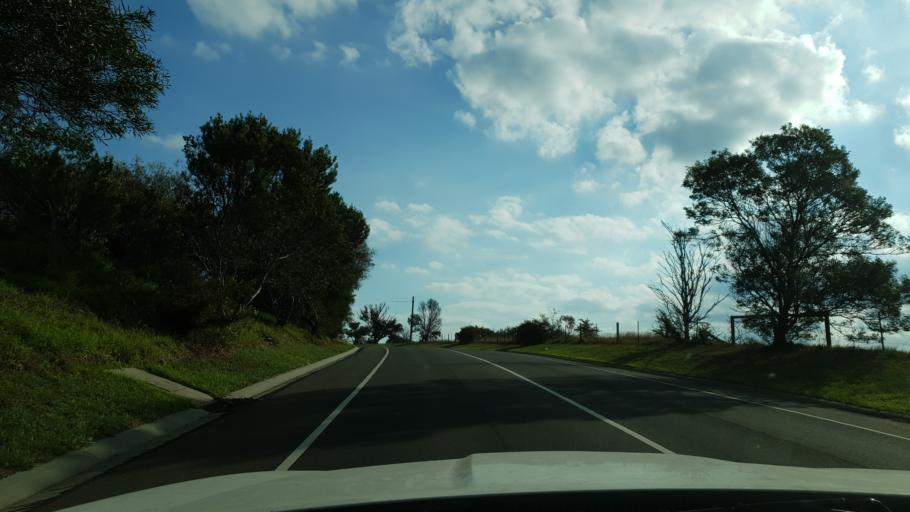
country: AU
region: Victoria
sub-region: East Gippsland
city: Bairnsdale
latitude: -37.8167
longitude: 147.6132
